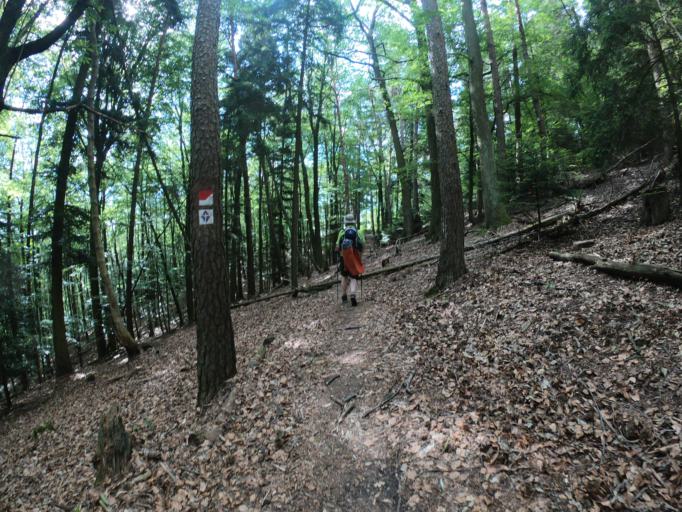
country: DE
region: Rheinland-Pfalz
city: Gleiszellen-Gleishorbach
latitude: 49.1295
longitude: 7.9892
